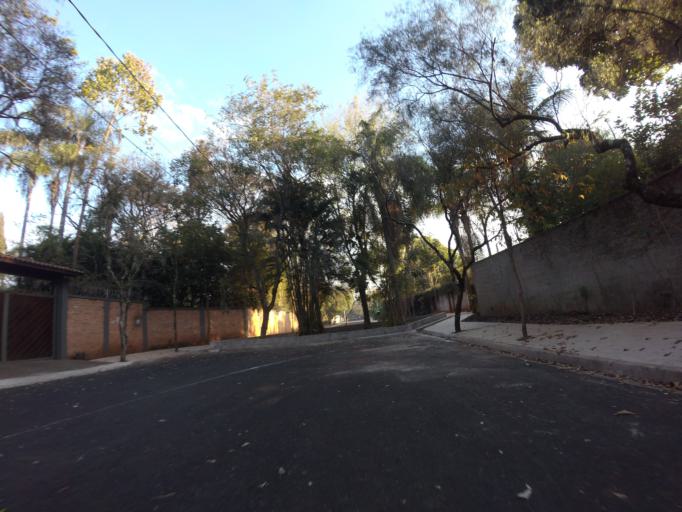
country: BR
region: Sao Paulo
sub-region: Piracicaba
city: Piracicaba
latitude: -22.7550
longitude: -47.5912
